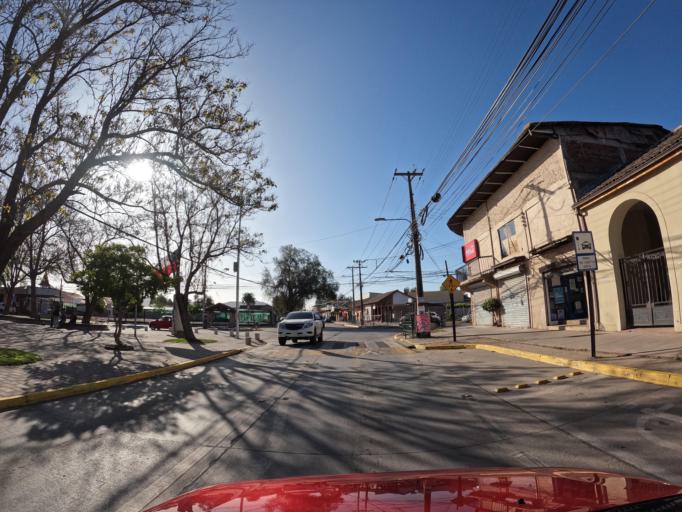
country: CL
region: O'Higgins
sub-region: Provincia de Colchagua
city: Santa Cruz
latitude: -34.7281
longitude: -71.2736
